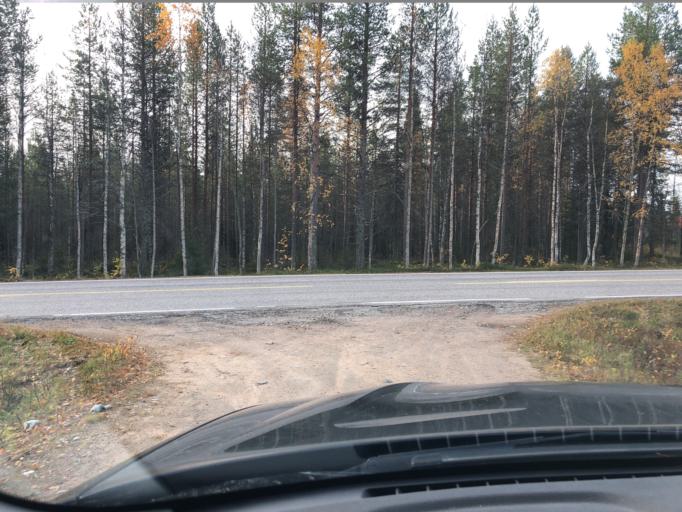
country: FI
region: Lapland
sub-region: Itae-Lappi
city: Posio
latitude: 66.0806
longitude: 28.5235
